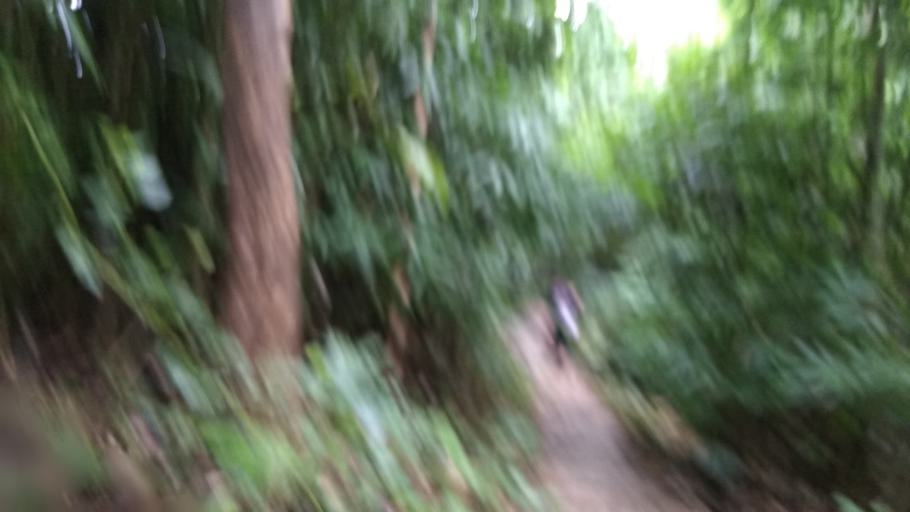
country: IN
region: Tripura
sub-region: Dhalai
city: Kamalpur
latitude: 24.1701
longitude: 91.8991
